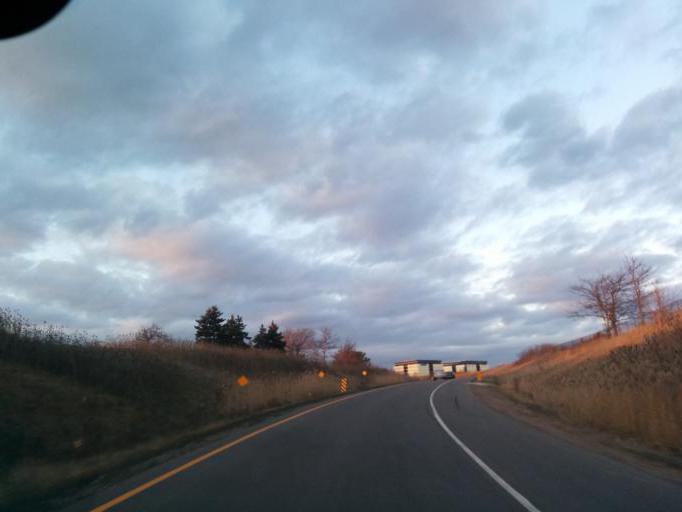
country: CA
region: Ontario
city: Oakville
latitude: 43.4965
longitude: -79.6719
